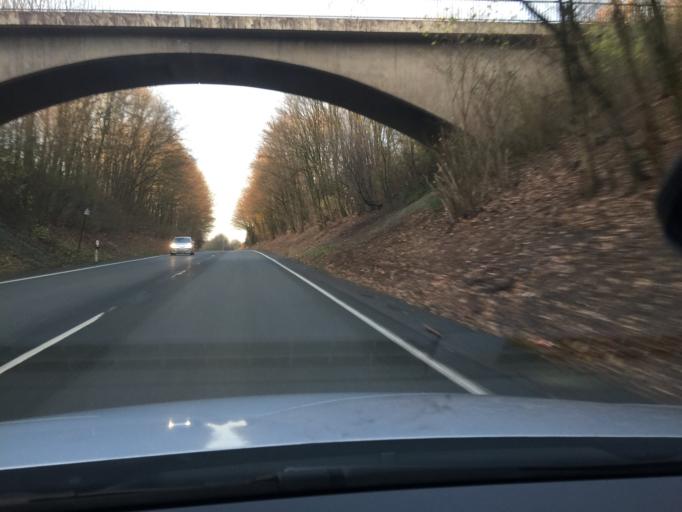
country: DE
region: North Rhine-Westphalia
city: Sprockhovel
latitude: 51.3359
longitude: 7.2183
